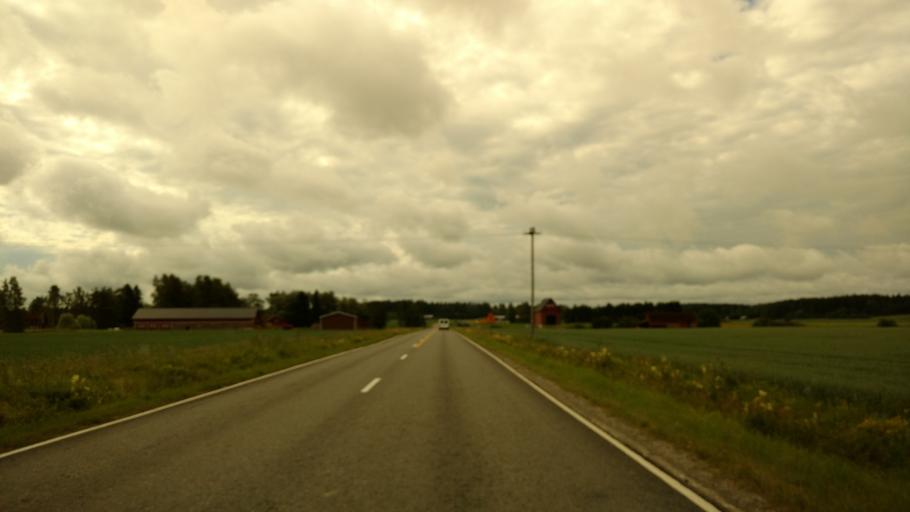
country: FI
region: Varsinais-Suomi
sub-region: Salo
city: Kuusjoki
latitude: 60.5167
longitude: 23.1791
